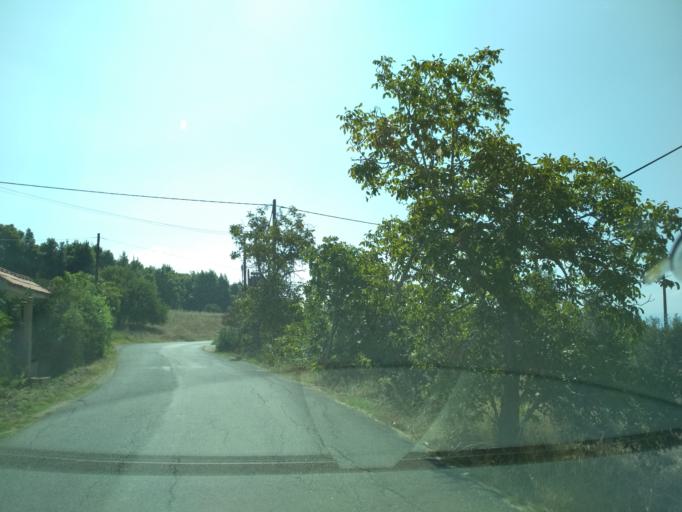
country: GR
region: Central Greece
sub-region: Nomos Evvoias
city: Roviai
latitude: 38.8233
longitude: 23.2465
